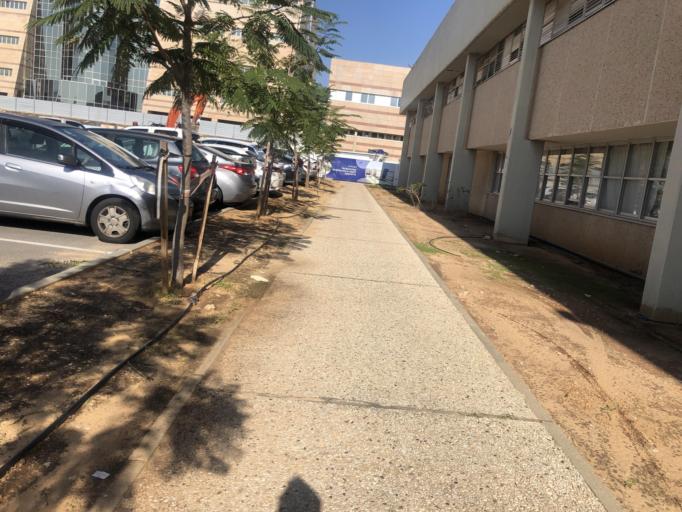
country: IL
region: Tel Aviv
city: Or Yehuda
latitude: 32.0451
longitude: 34.8453
